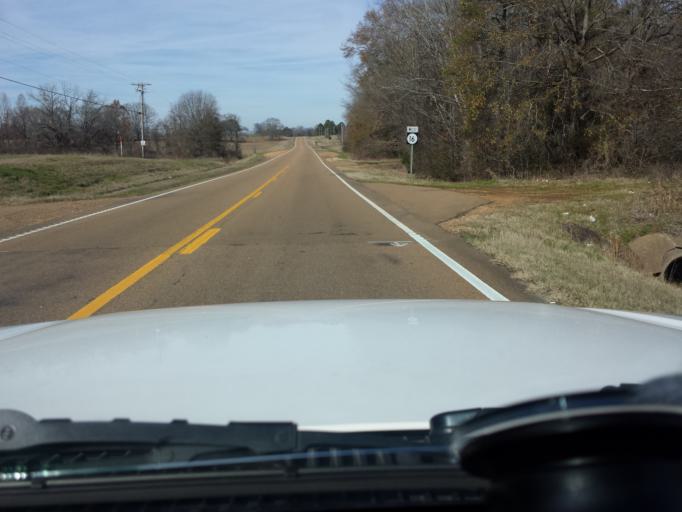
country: US
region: Mississippi
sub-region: Madison County
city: Canton
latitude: 32.6843
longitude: -90.0592
